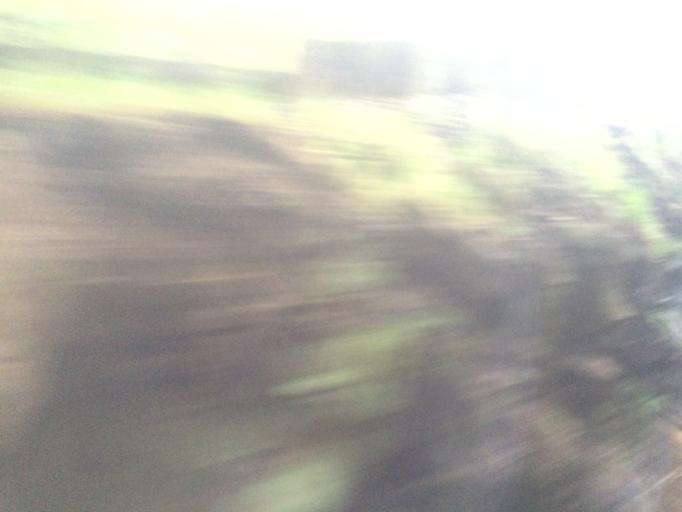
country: GB
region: Scotland
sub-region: Stirling
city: Dunblane
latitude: 56.2006
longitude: -3.9626
